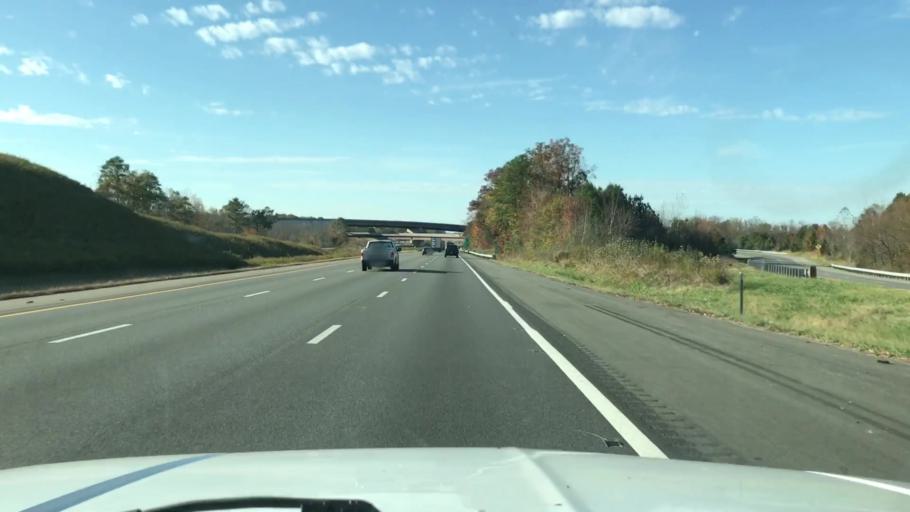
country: US
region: Virginia
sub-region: Henrico County
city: Short Pump
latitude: 37.6696
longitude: -77.6447
